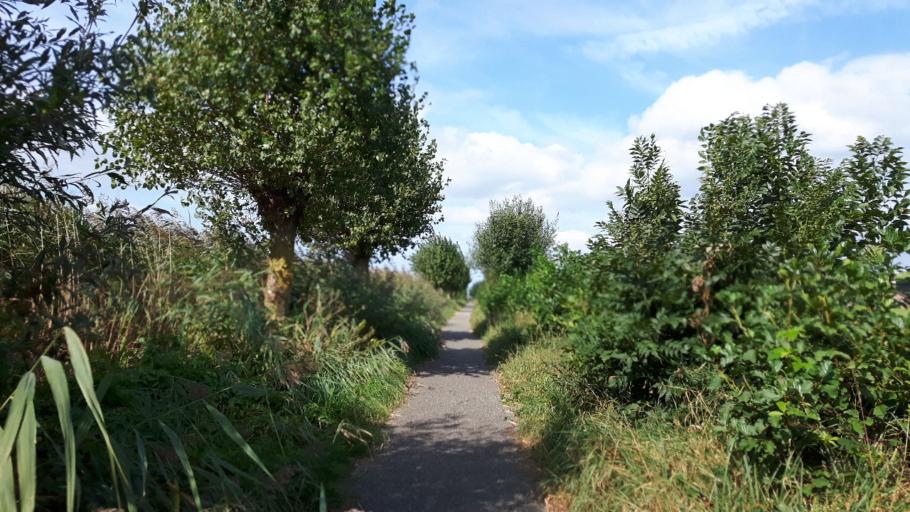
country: NL
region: Utrecht
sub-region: Gemeente Woerden
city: Woerden
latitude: 52.1243
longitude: 4.8378
